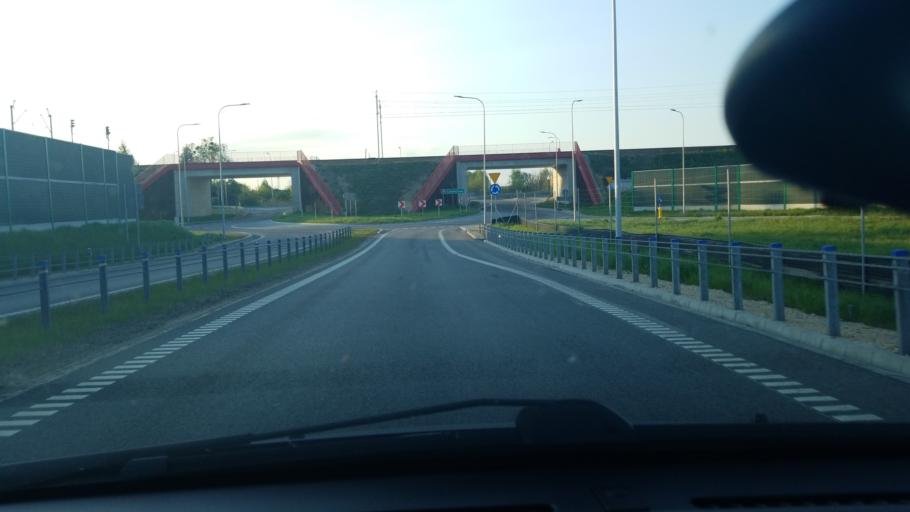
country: PL
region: Silesian Voivodeship
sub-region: Powiat czestochowski
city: Blachownia
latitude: 50.7840
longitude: 19.0100
